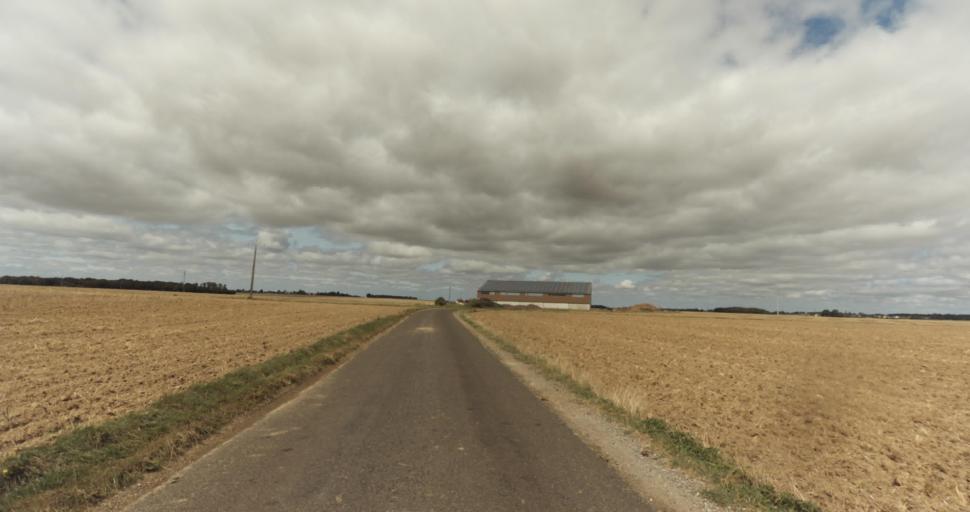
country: FR
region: Haute-Normandie
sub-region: Departement de l'Eure
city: La Madeleine-de-Nonancourt
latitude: 48.9034
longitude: 1.2361
